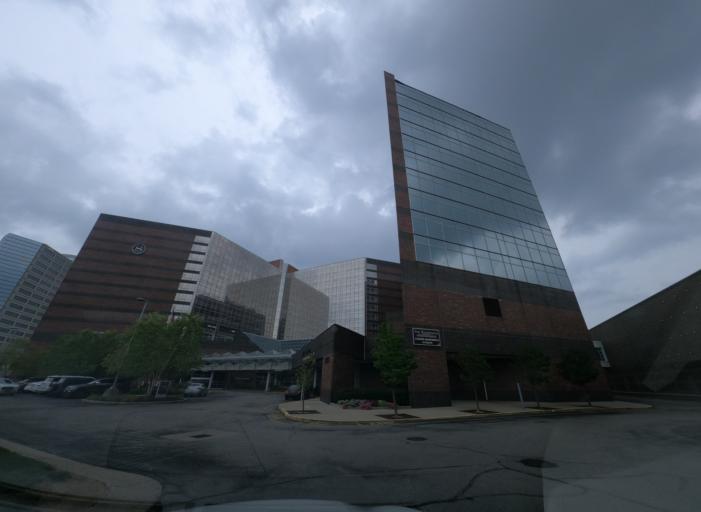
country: US
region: Indiana
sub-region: Marion County
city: Meridian Hills
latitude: 39.9148
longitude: -86.1091
